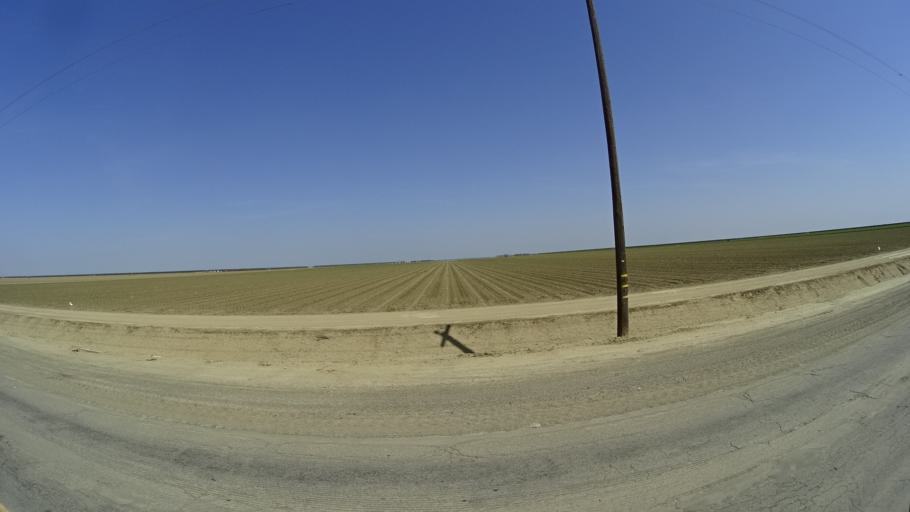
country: US
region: California
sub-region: Kings County
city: Kettleman City
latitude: 36.1377
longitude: -119.9665
